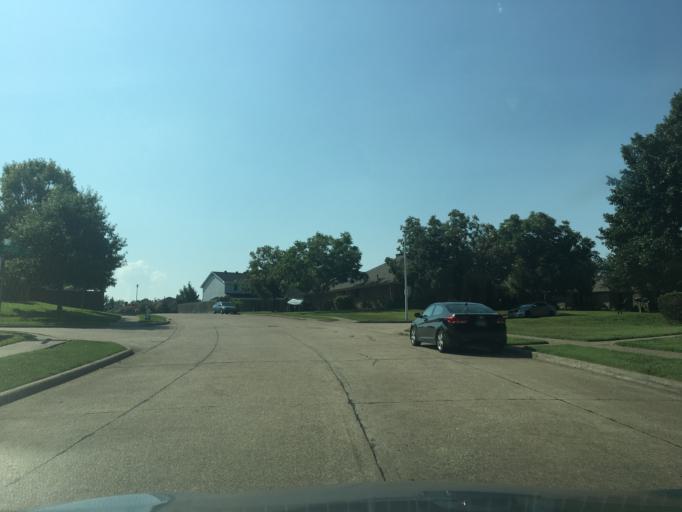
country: US
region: Texas
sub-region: Dallas County
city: Garland
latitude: 32.9498
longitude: -96.6324
